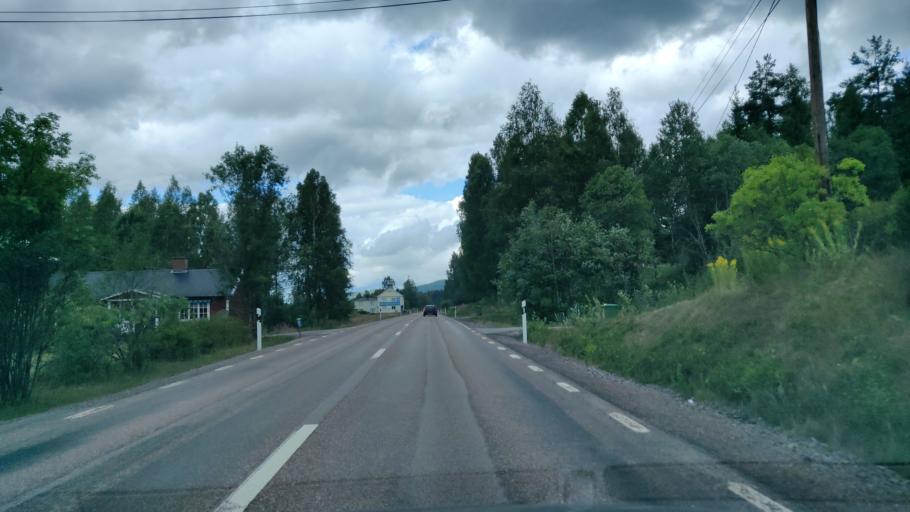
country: SE
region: Vaermland
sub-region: Torsby Kommun
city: Torsby
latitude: 60.5889
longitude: 13.0770
